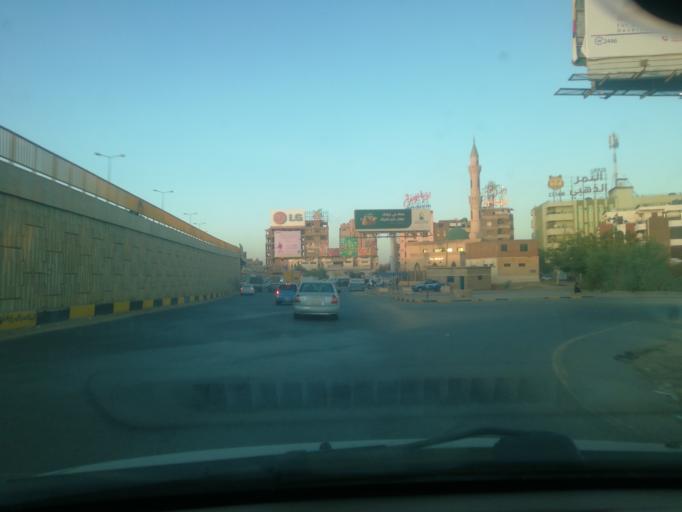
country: SD
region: Khartoum
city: Khartoum
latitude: 15.6230
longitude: 32.5553
